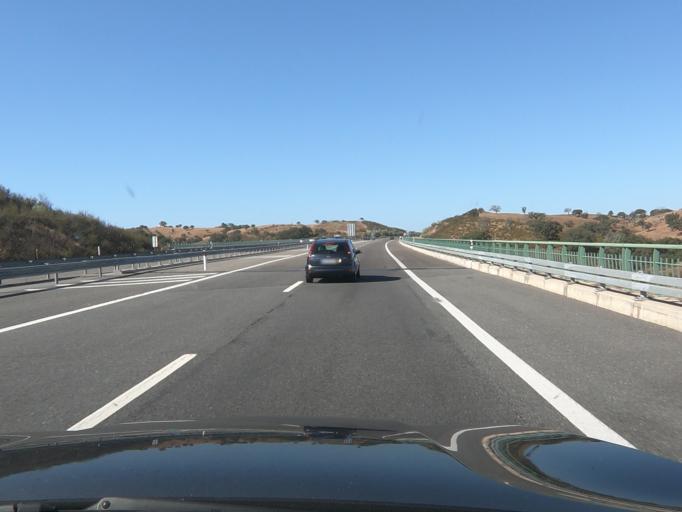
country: PT
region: Beja
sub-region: Almodovar
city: Almodovar
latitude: 37.5092
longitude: -8.1871
